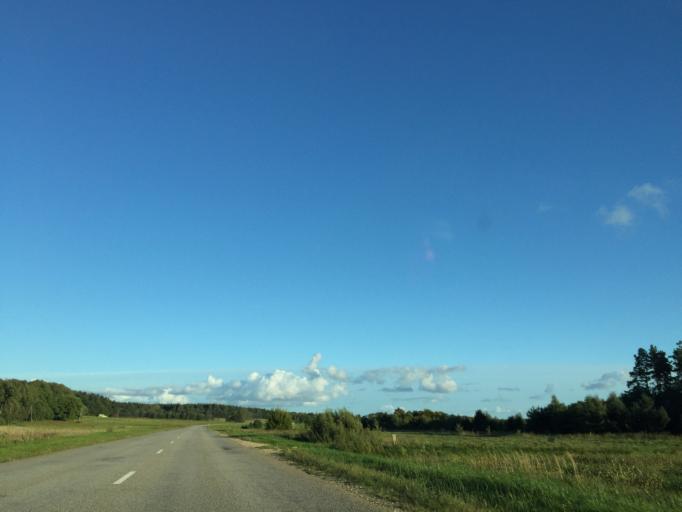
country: LV
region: Kuldigas Rajons
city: Kuldiga
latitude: 56.9306
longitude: 22.0422
